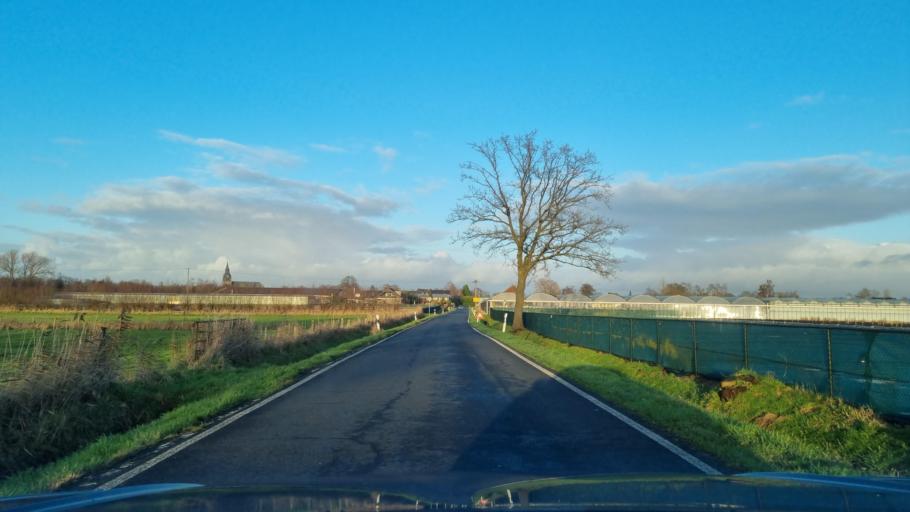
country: DE
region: North Rhine-Westphalia
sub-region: Regierungsbezirk Dusseldorf
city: Kranenburg
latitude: 51.7822
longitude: 6.0028
